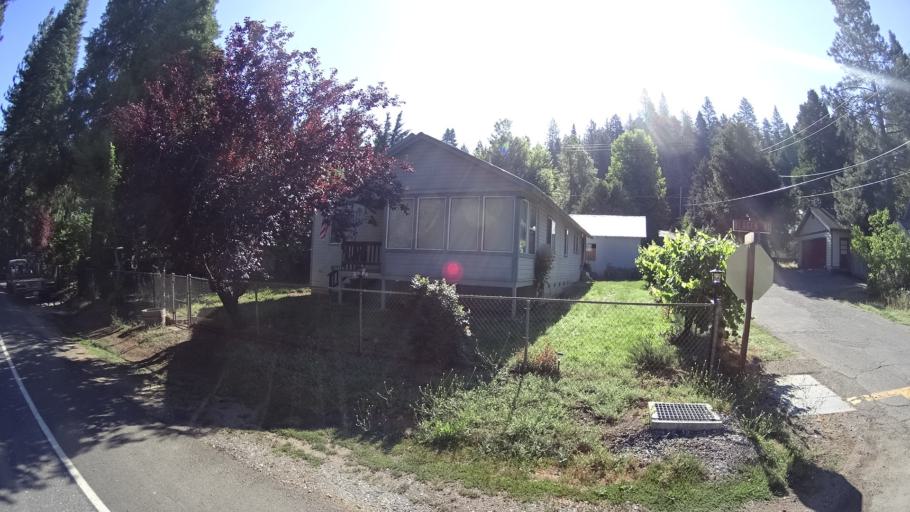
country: US
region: California
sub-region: Calaveras County
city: Arnold
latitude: 38.2647
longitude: -120.3414
